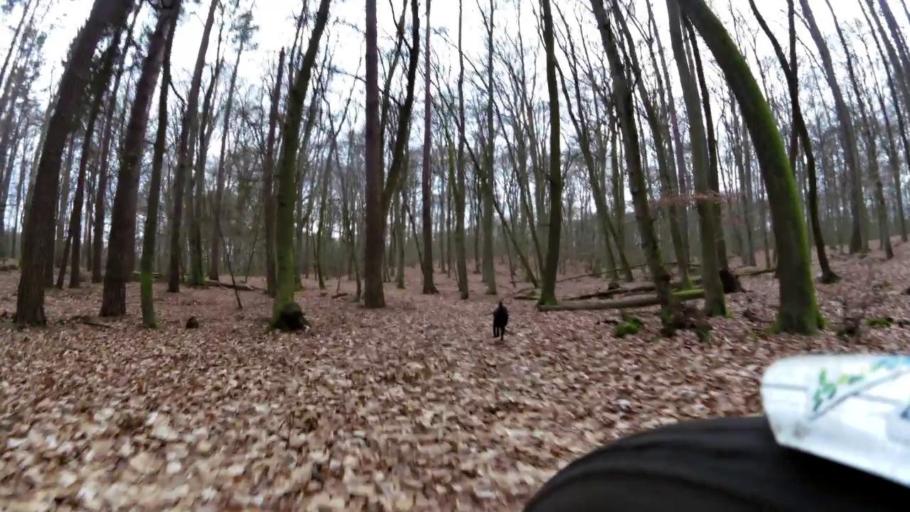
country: PL
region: West Pomeranian Voivodeship
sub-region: Powiat kamienski
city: Miedzyzdroje
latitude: 53.9387
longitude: 14.5521
